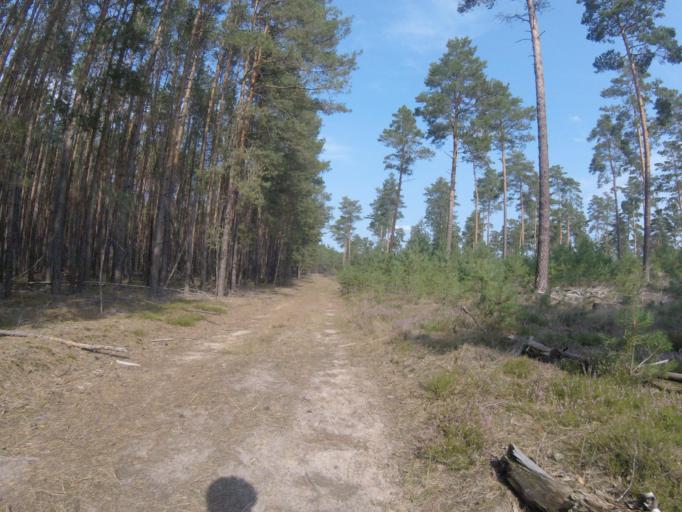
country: DE
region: Brandenburg
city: Bestensee
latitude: 52.2727
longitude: 13.7028
